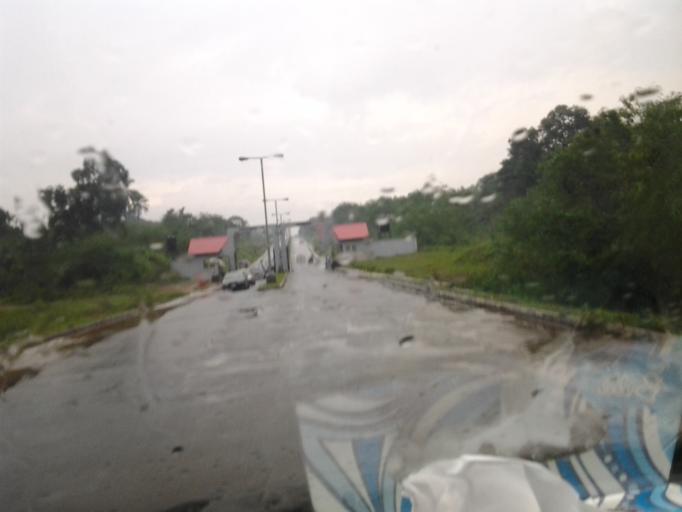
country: NG
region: Oyo
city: Moniya
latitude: 7.4604
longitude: 3.8988
